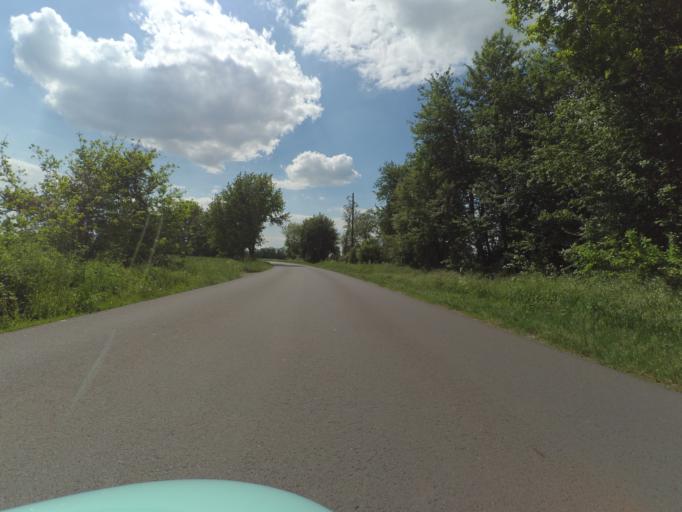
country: DE
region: Lower Saxony
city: Muden
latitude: 52.5121
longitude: 10.3689
